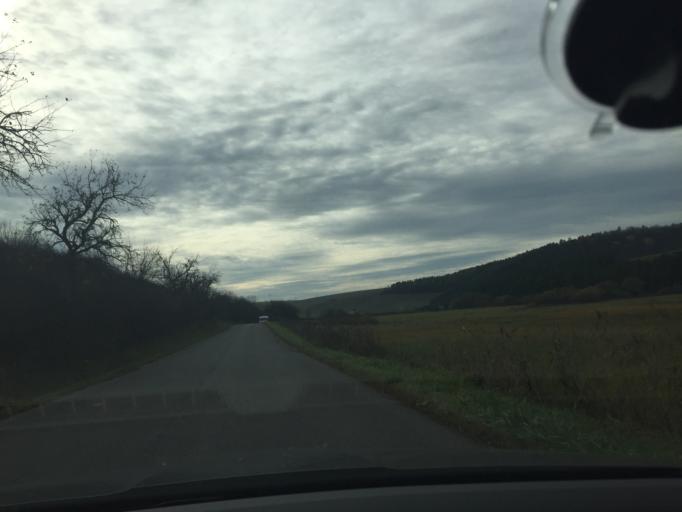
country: SK
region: Presovsky
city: Spisske Podhradie
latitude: 48.9739
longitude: 20.7916
